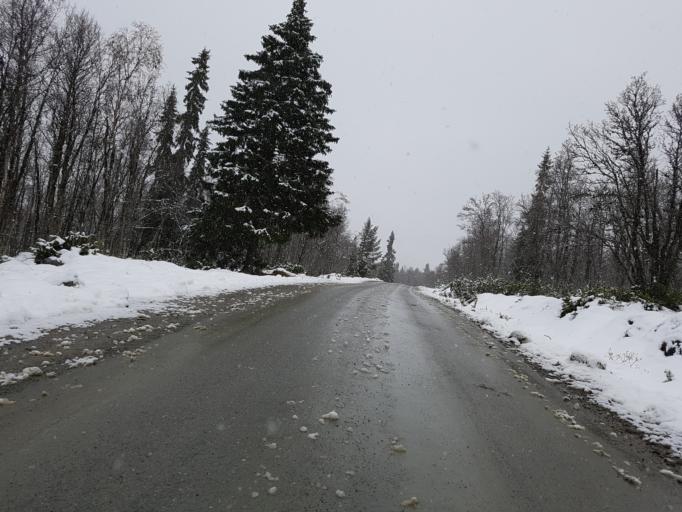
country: NO
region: Oppland
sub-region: Sel
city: Otta
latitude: 61.7918
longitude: 9.7185
